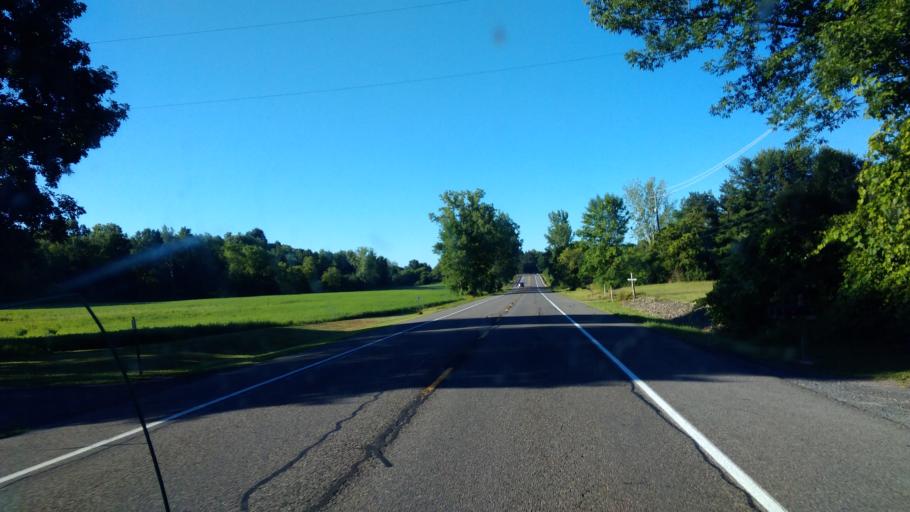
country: US
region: New York
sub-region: Wayne County
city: Lyons
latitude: 42.9890
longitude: -76.9782
